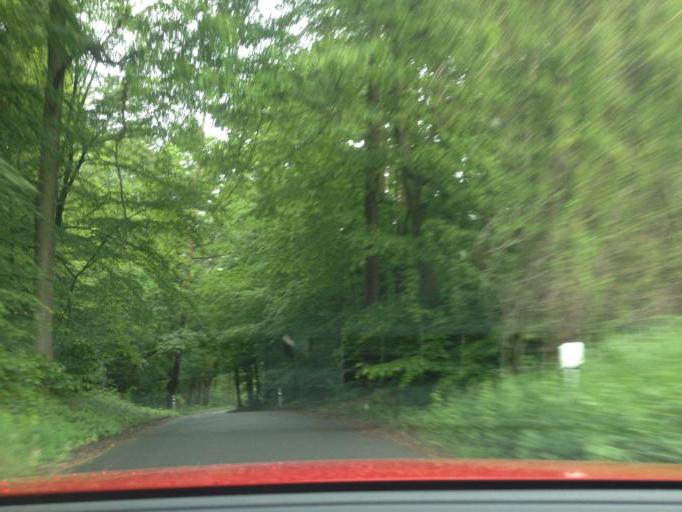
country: DE
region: Bavaria
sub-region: Regierungsbezirk Mittelfranken
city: Lauf an der Pegnitz
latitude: 49.4798
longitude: 11.2876
